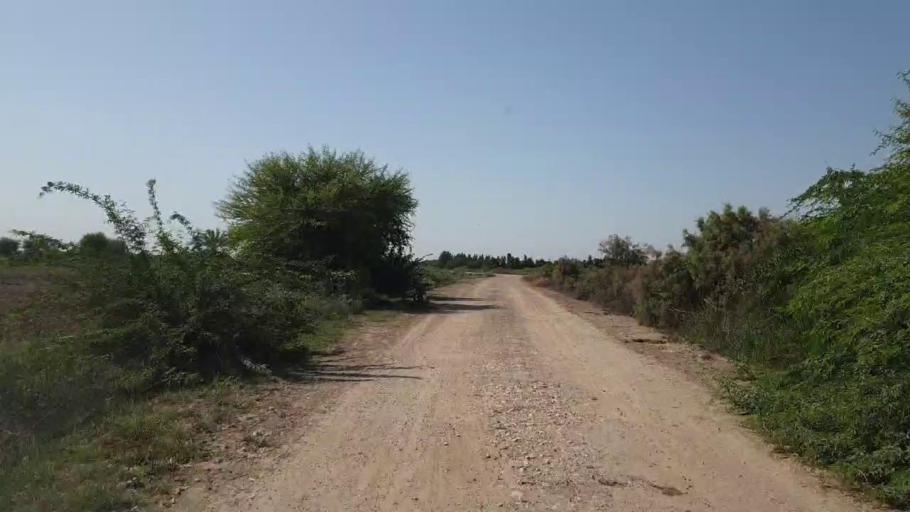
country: PK
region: Sindh
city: Tando Bago
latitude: 24.7056
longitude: 69.0424
